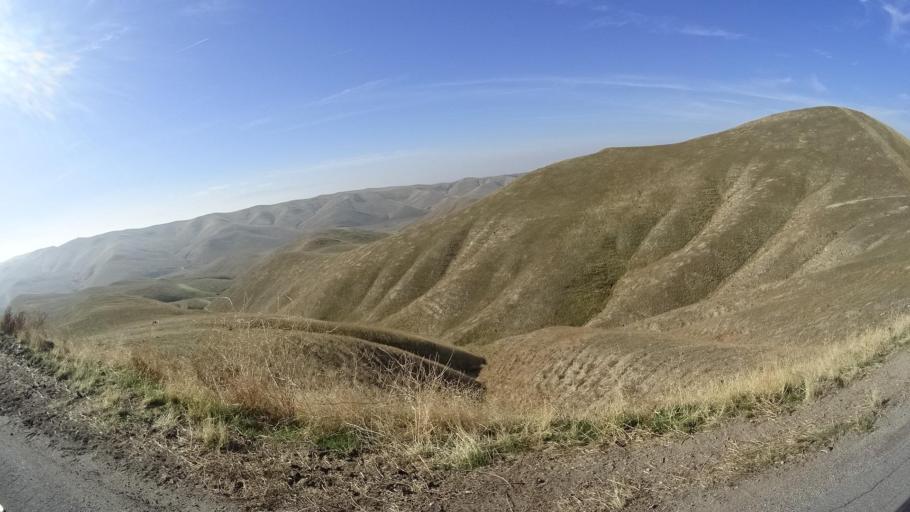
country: US
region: California
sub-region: Kern County
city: Lamont
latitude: 35.3994
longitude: -118.7795
